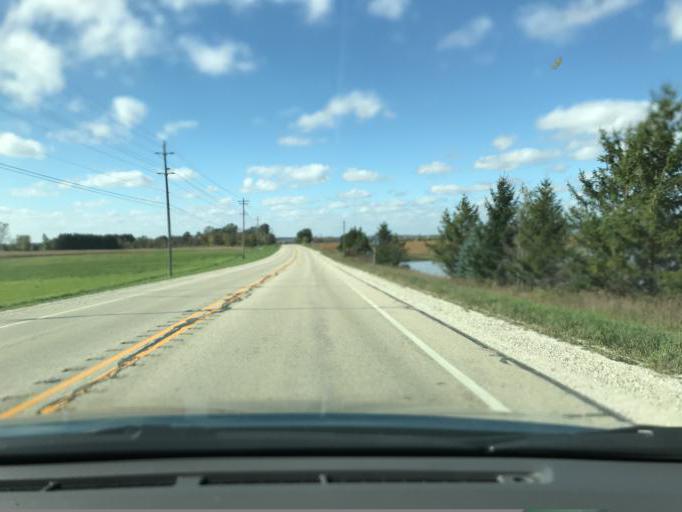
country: US
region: Wisconsin
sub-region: Racine County
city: Union Grove
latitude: 42.6288
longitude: -88.0101
